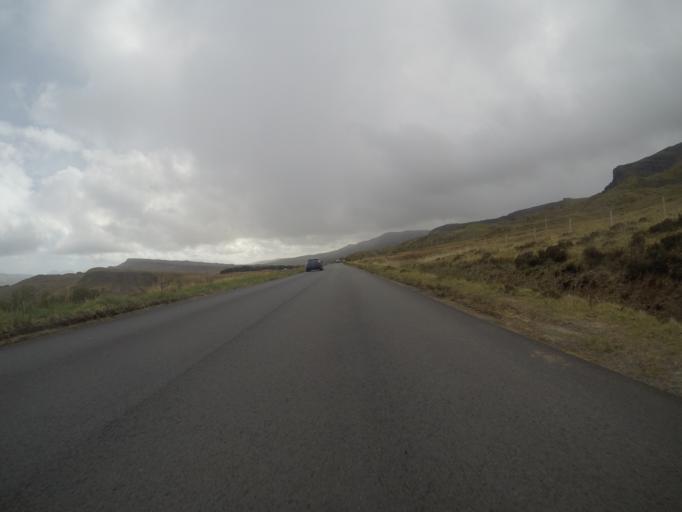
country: GB
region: Scotland
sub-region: Highland
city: Portree
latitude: 57.5020
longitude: -6.1546
